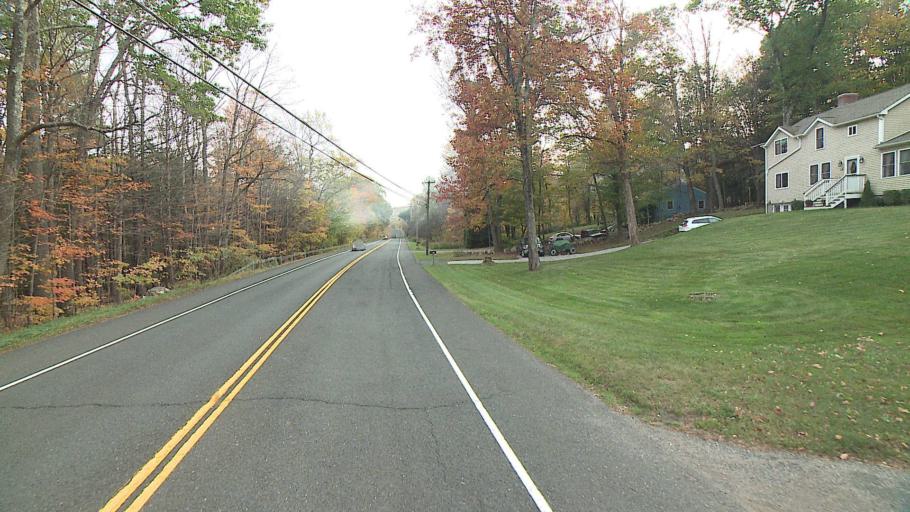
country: US
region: Connecticut
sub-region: Litchfield County
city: Winchester Center
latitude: 41.9513
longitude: -73.1148
